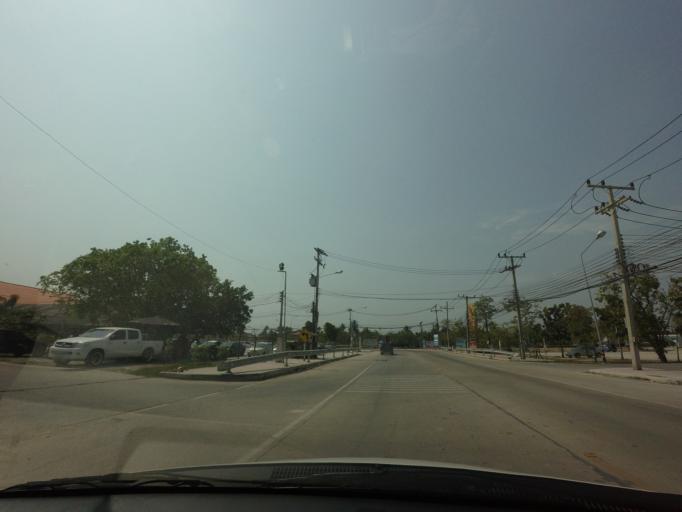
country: TH
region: Nakhon Pathom
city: Sam Phran
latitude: 13.7462
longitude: 100.2611
